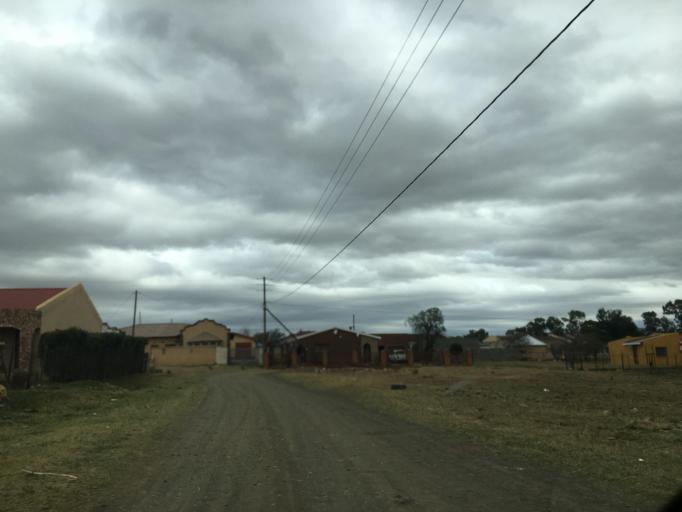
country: ZA
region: Eastern Cape
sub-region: Chris Hani District Municipality
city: Cala
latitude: -31.5335
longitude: 27.6912
